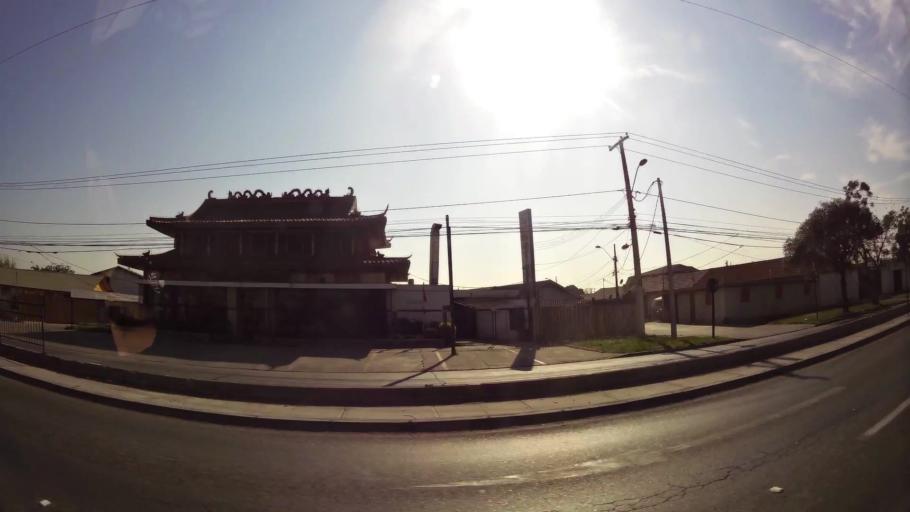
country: CL
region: Santiago Metropolitan
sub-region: Provincia de Santiago
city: Lo Prado
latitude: -33.5124
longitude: -70.7199
